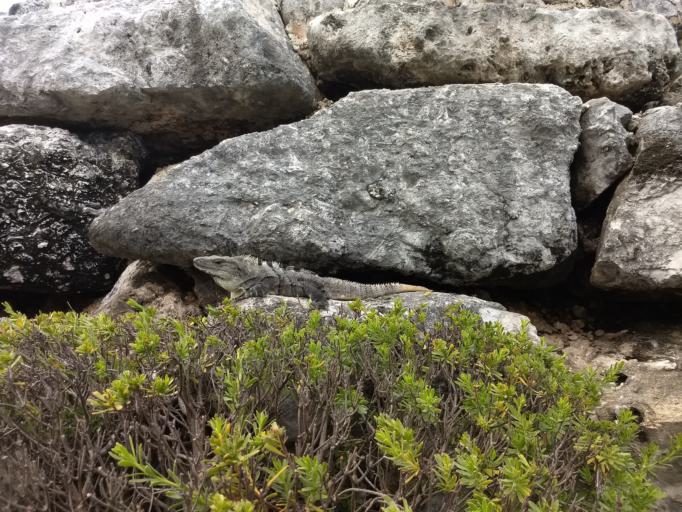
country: MX
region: Quintana Roo
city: Playa del Carmen
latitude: 20.5072
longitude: -87.2124
